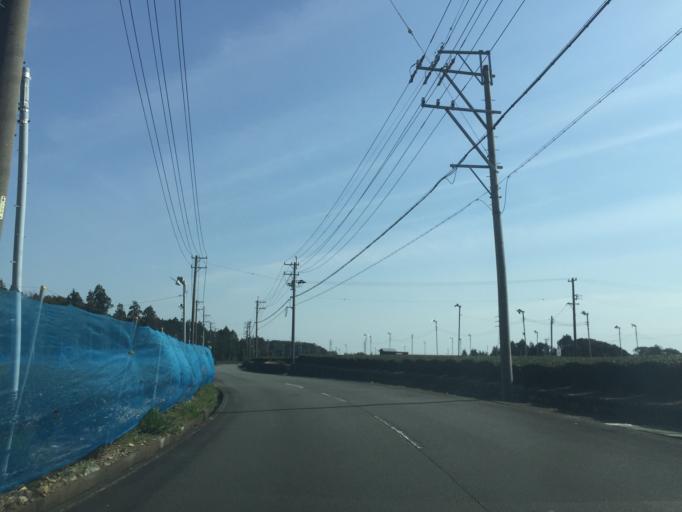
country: JP
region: Shizuoka
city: Kanaya
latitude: 34.8234
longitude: 138.1136
